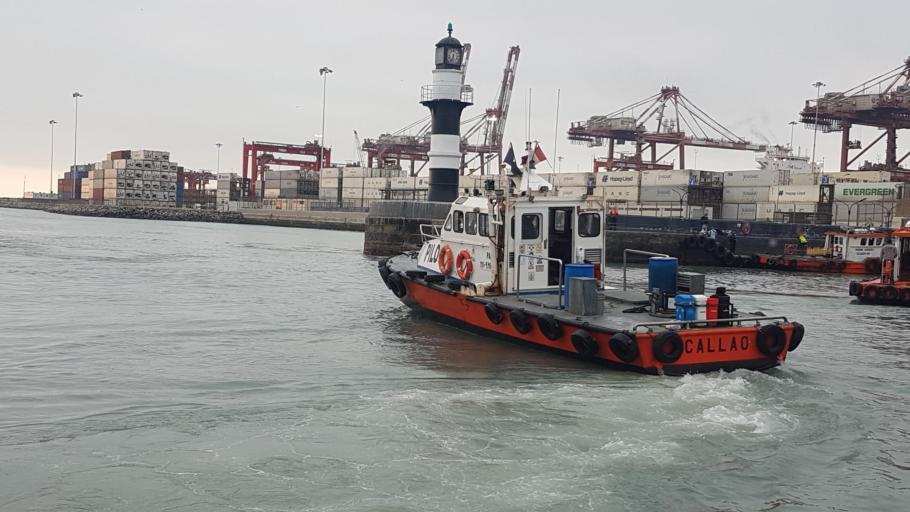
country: PE
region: Callao
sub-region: Callao
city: Callao
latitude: -12.0587
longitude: -77.1489
